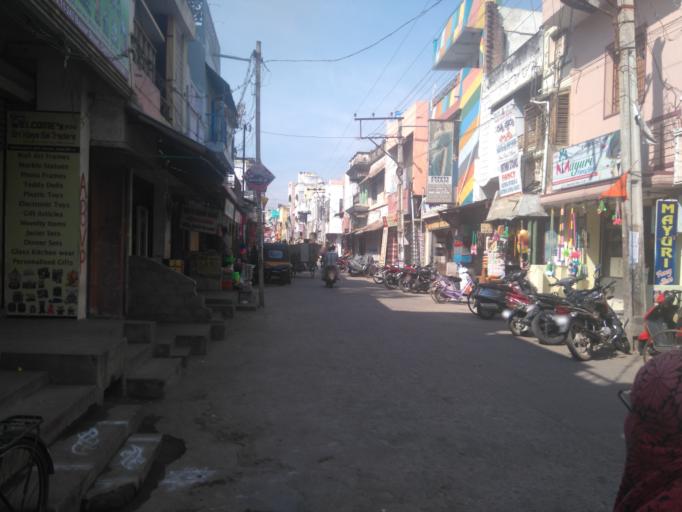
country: IN
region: Andhra Pradesh
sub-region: Chittoor
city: Chittoor
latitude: 13.2193
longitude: 79.0979
